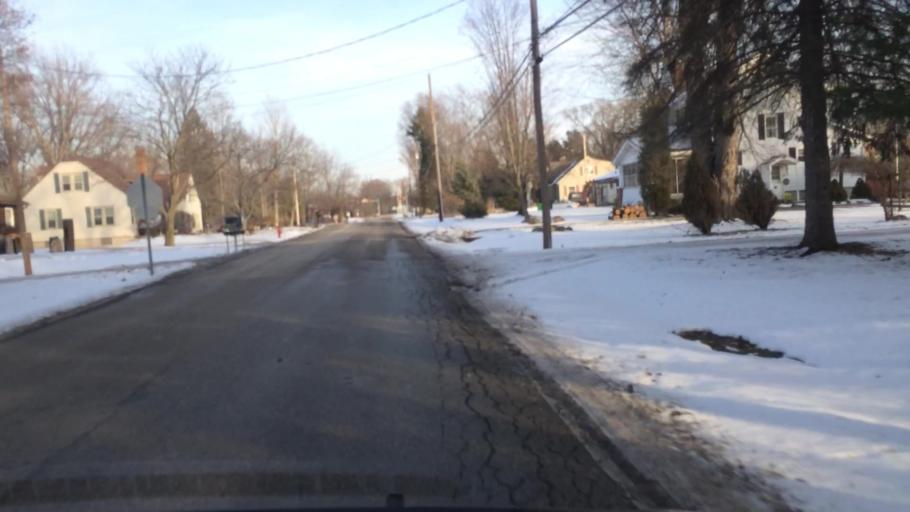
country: US
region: Ohio
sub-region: Summit County
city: Stow
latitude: 41.1749
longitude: -81.4442
